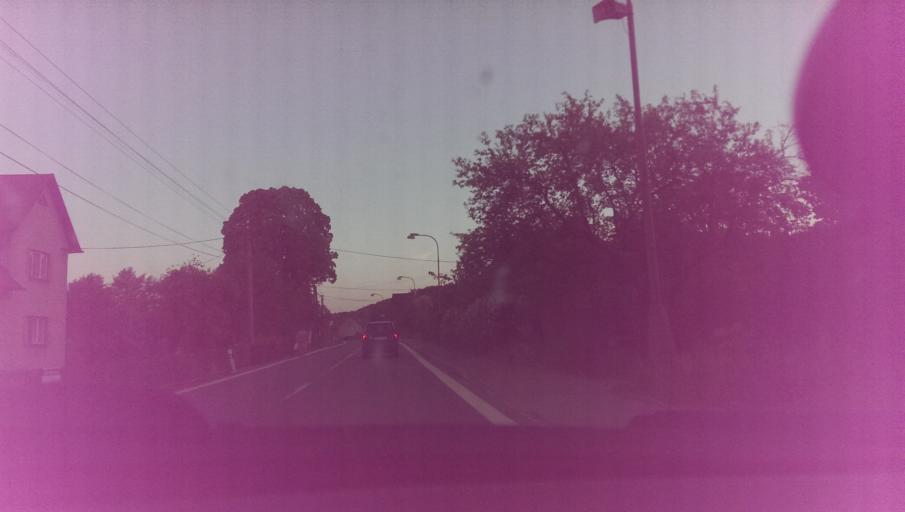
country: CZ
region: Zlin
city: Valasska Polanka
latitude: 49.2893
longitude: 17.9986
